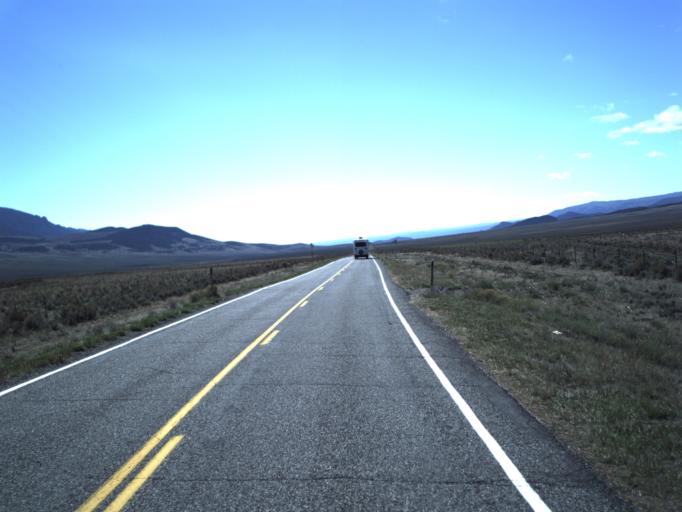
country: US
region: Utah
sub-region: Wayne County
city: Loa
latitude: 38.4220
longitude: -111.9228
